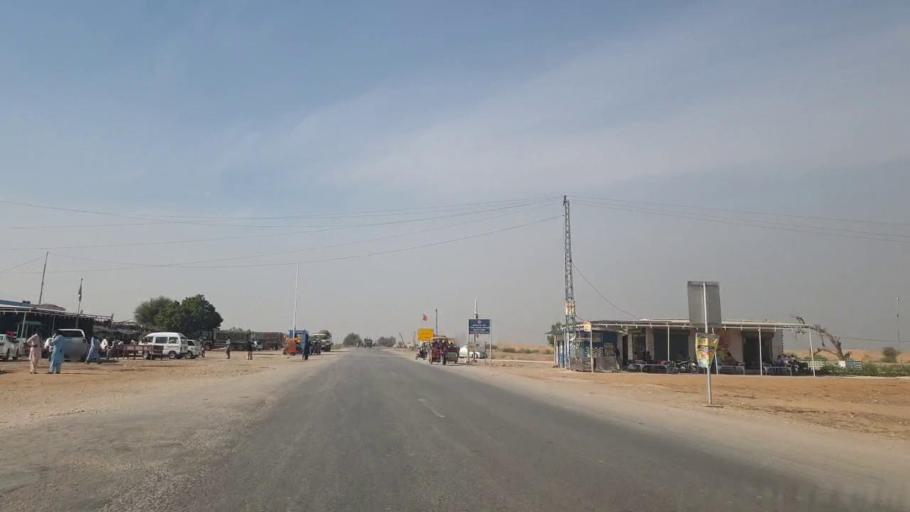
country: PK
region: Sindh
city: Sann
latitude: 26.0281
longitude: 68.1252
